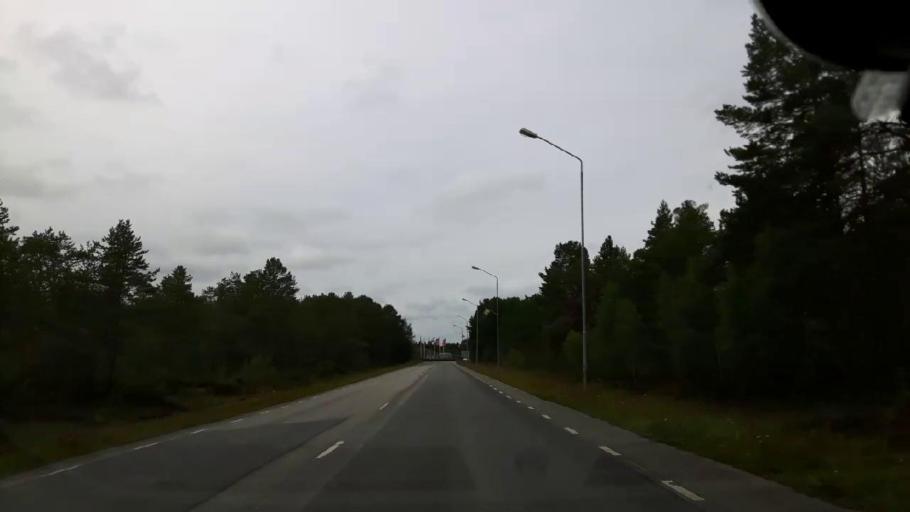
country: SE
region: Jaemtland
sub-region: OEstersunds Kommun
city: Ostersund
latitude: 63.1709
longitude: 14.5705
